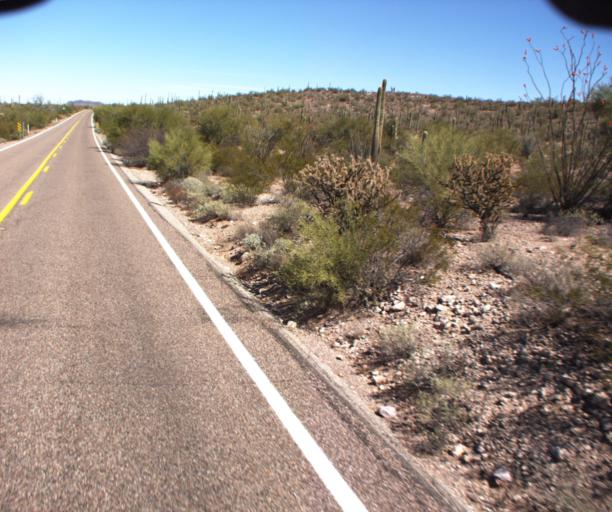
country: MX
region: Sonora
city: Sonoyta
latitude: 32.0143
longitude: -112.8044
